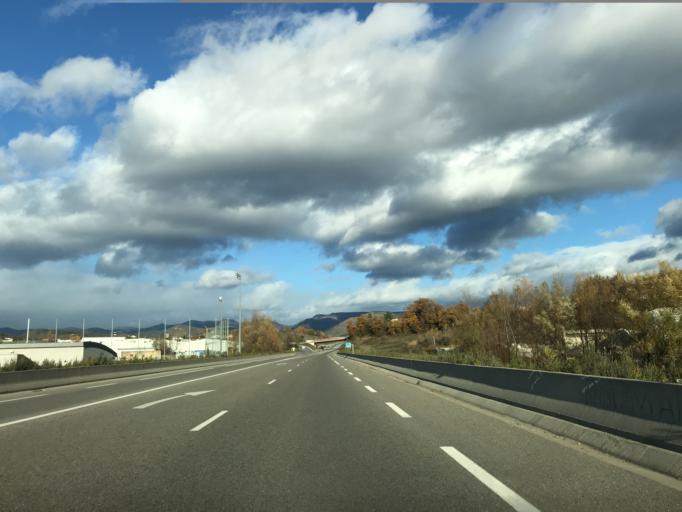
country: FR
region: Rhone-Alpes
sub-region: Departement de l'Ardeche
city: Saint-Etienne-de-Fontbellon
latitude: 44.6025
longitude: 4.3978
